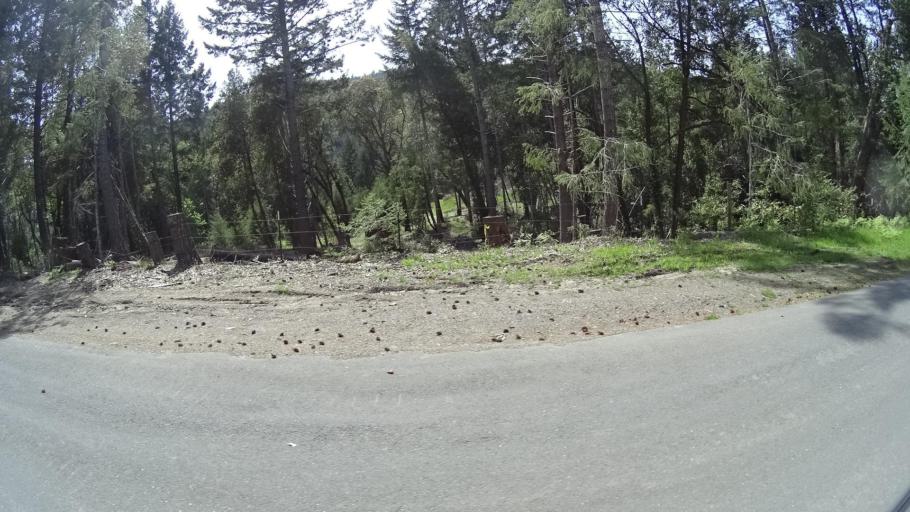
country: US
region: California
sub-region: Humboldt County
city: Redway
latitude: 40.3727
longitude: -123.7377
